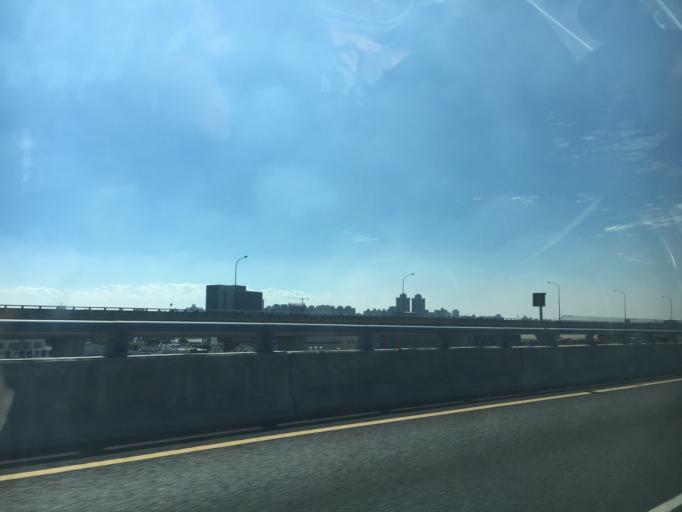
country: TW
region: Taiwan
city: Taoyuan City
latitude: 25.0406
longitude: 121.3015
